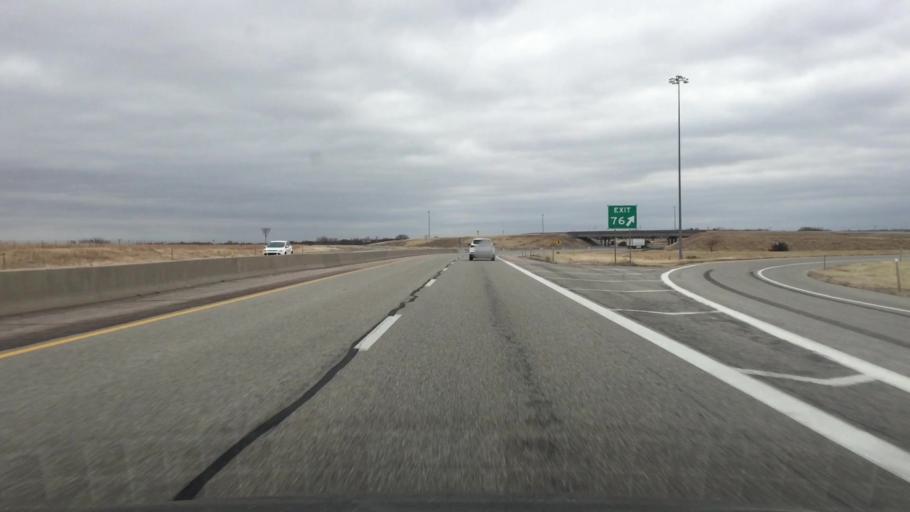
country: US
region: Kansas
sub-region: Butler County
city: El Dorado
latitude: 37.8789
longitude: -96.8438
